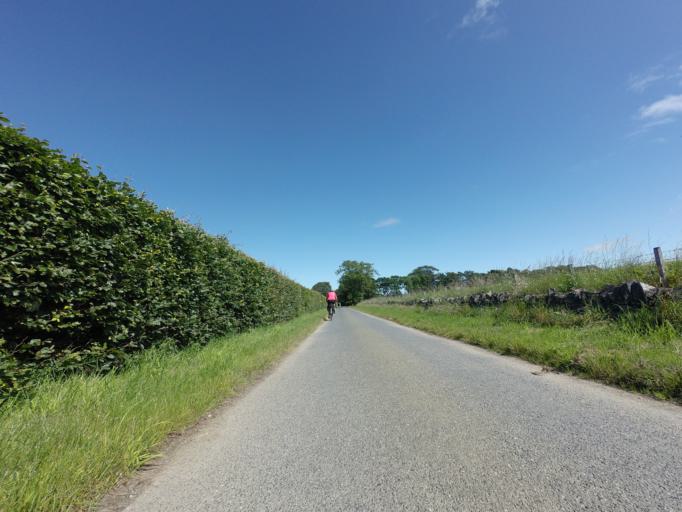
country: GB
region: Scotland
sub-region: Aberdeenshire
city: Banff
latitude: 57.6202
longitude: -2.5057
